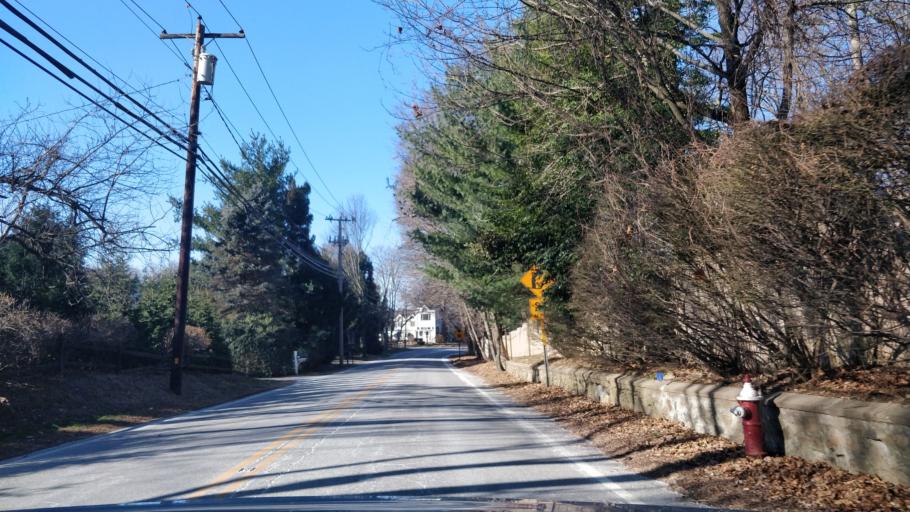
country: US
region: New York
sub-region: Nassau County
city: East Hills
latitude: 40.7915
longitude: -73.6159
